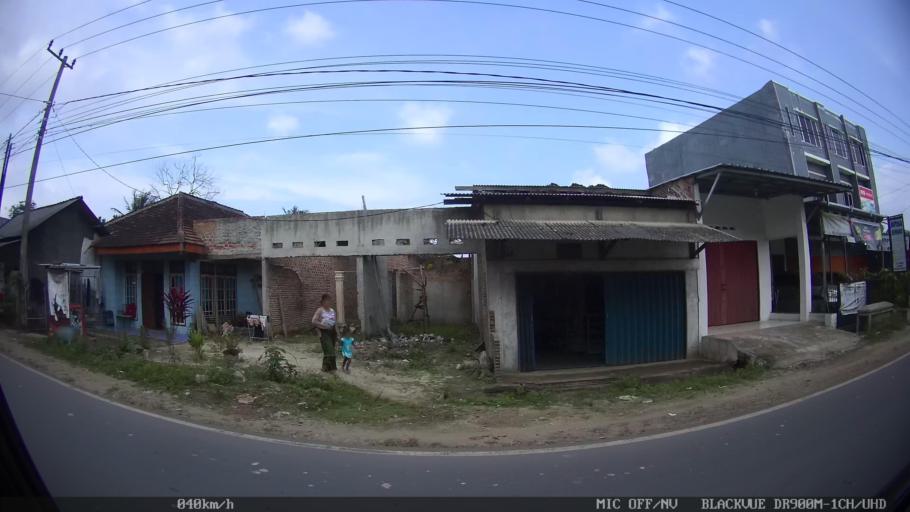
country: ID
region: Lampung
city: Kedaton
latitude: -5.3289
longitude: 105.2902
